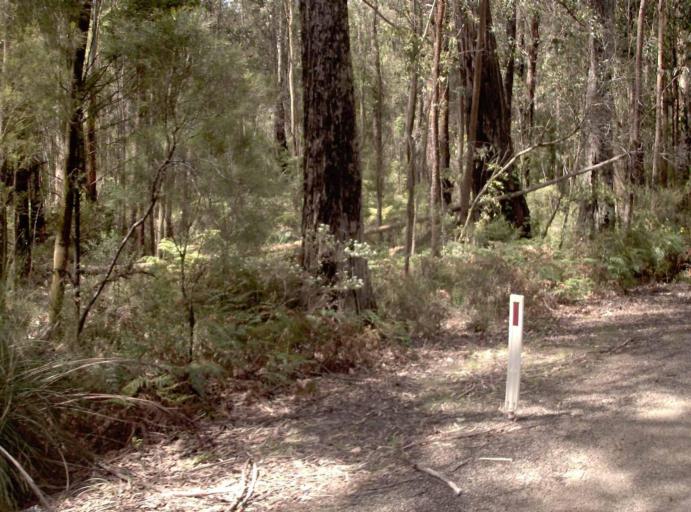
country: AU
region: New South Wales
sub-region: Bombala
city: Bombala
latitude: -37.5351
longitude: 149.3745
